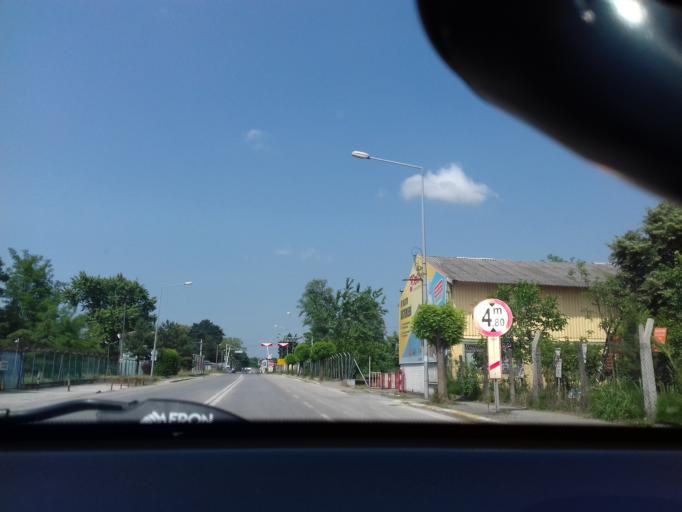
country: TR
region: Sakarya
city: Adapazari
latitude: 40.7274
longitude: 30.3754
